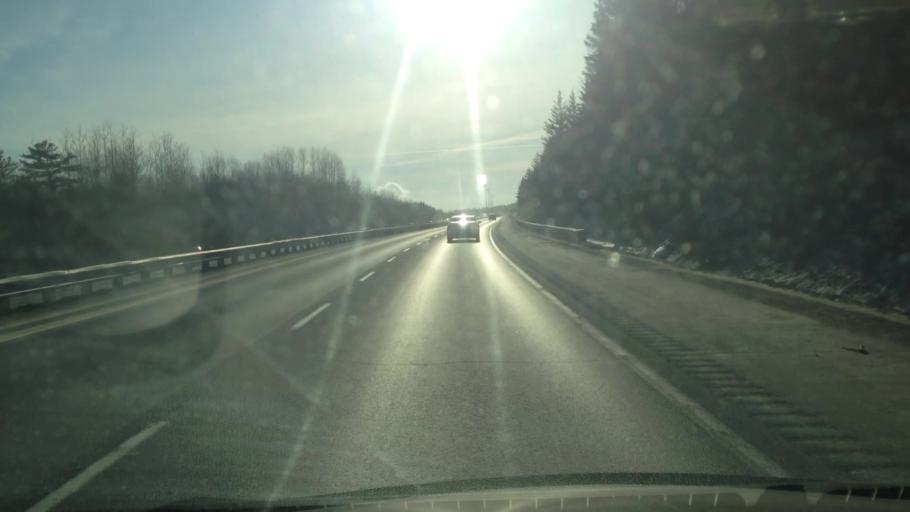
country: CA
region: Quebec
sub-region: Laurentides
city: Prevost
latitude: 45.8515
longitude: -74.0752
